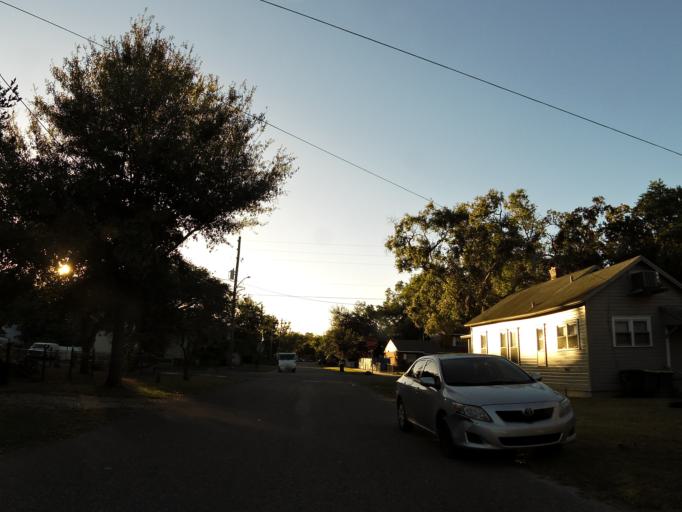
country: US
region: Florida
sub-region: Duval County
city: Jacksonville
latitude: 30.3398
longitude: -81.6464
